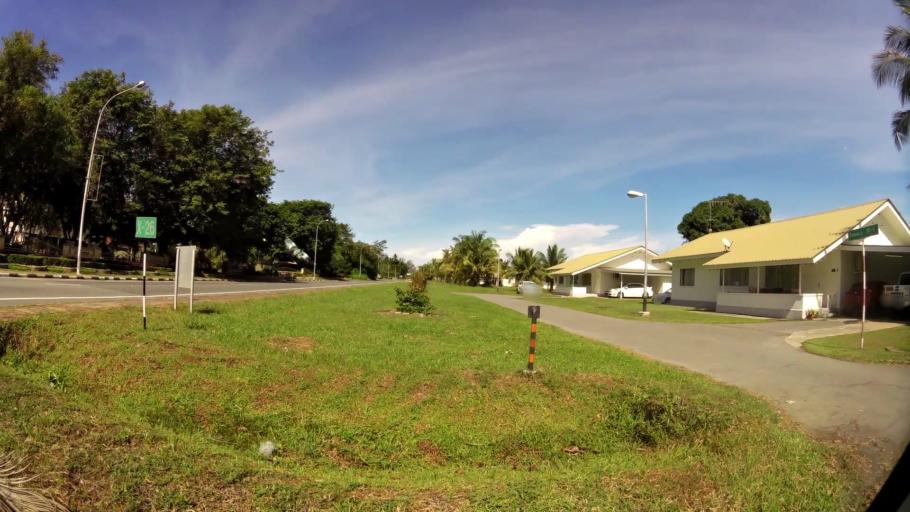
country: BN
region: Belait
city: Kuala Belait
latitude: 4.5883
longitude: 114.1958
